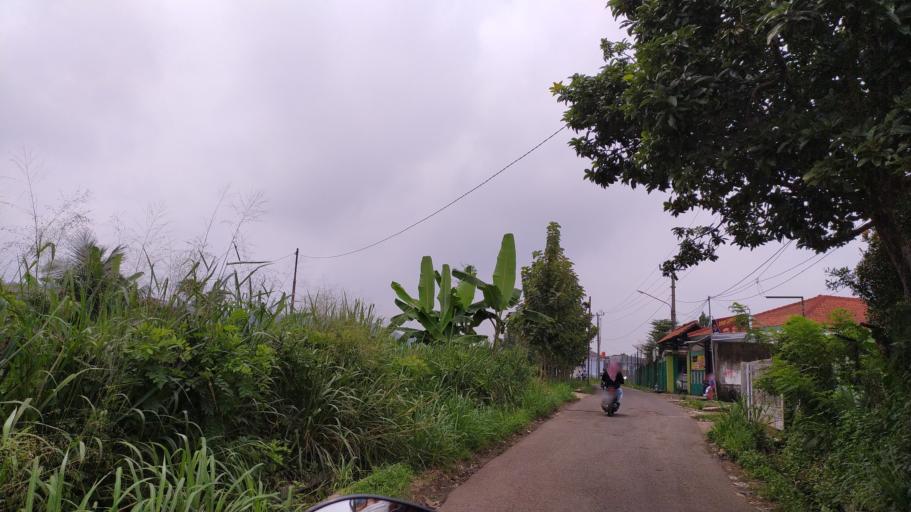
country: ID
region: West Java
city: Ciampea
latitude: -6.6126
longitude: 106.7099
